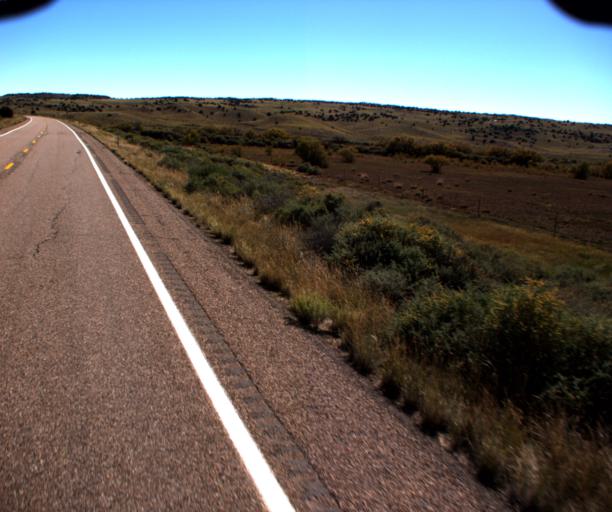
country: US
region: Arizona
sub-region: Apache County
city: Saint Johns
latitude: 34.5851
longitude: -109.5752
